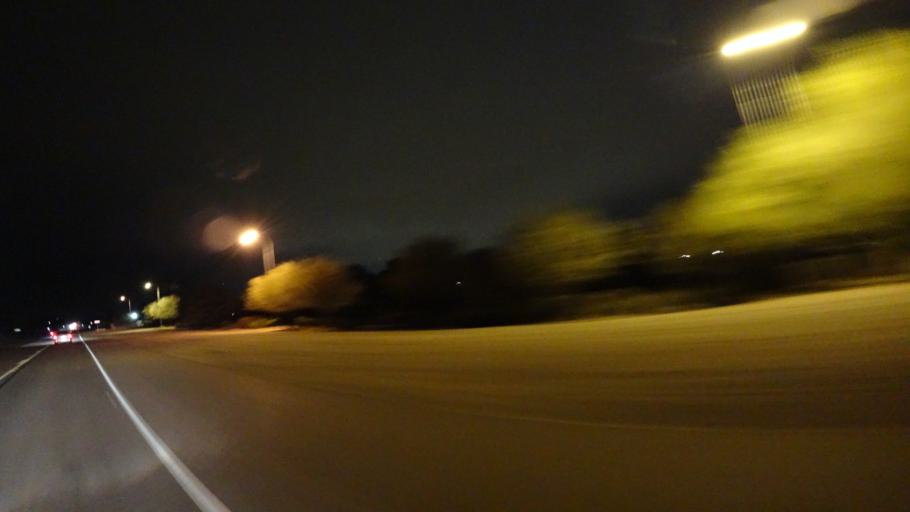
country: US
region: Arizona
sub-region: Maricopa County
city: Sun Lakes
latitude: 33.2337
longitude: -111.7940
